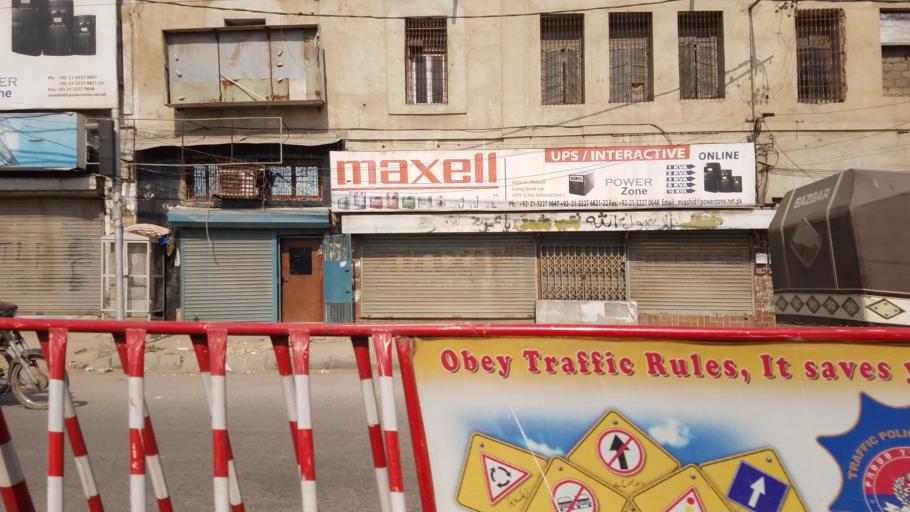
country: PK
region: Sindh
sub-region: Karachi District
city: Karachi
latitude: 24.8499
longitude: 67.0082
